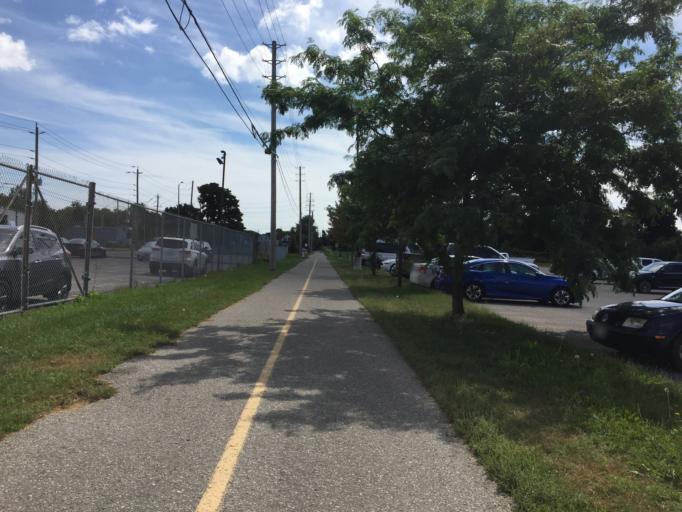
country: CA
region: Ontario
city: Oshawa
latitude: 43.8956
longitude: -78.8591
